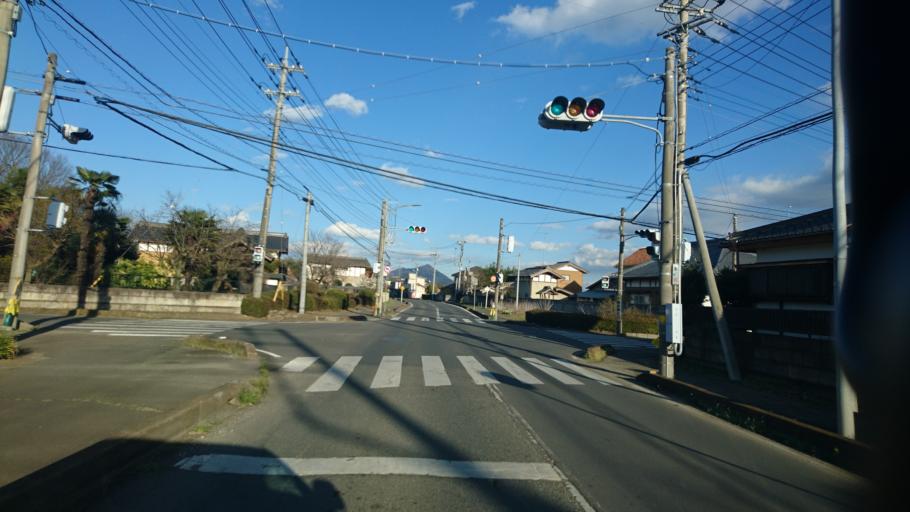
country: JP
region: Ibaraki
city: Shimodate
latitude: 36.2478
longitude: 139.9397
